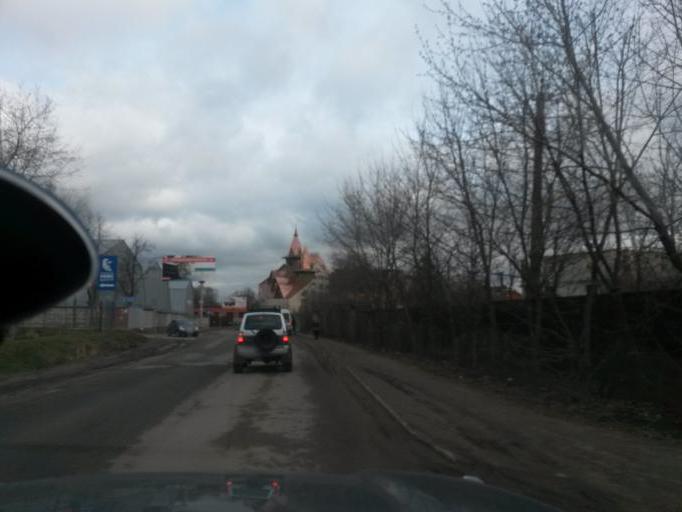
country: RU
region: Moscow
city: Zyablikovo
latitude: 55.6097
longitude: 37.7857
